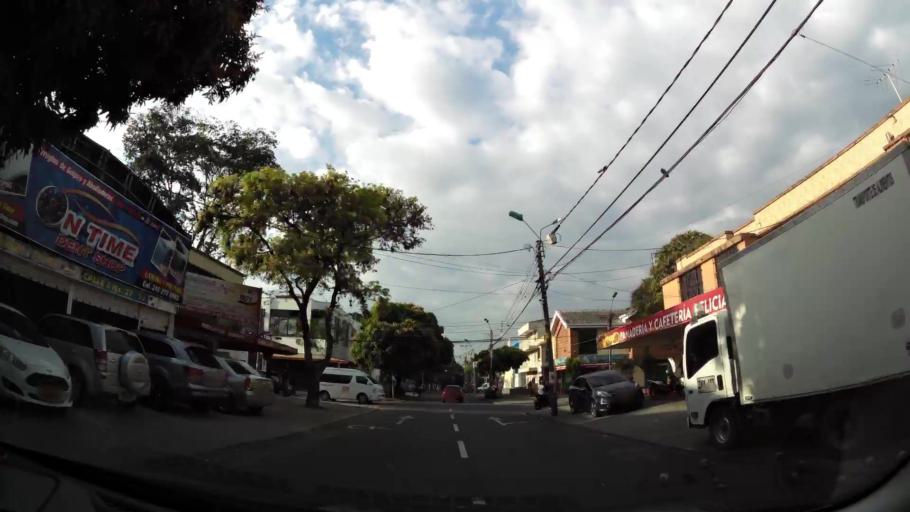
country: CO
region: Valle del Cauca
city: Cali
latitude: 3.4324
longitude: -76.5364
